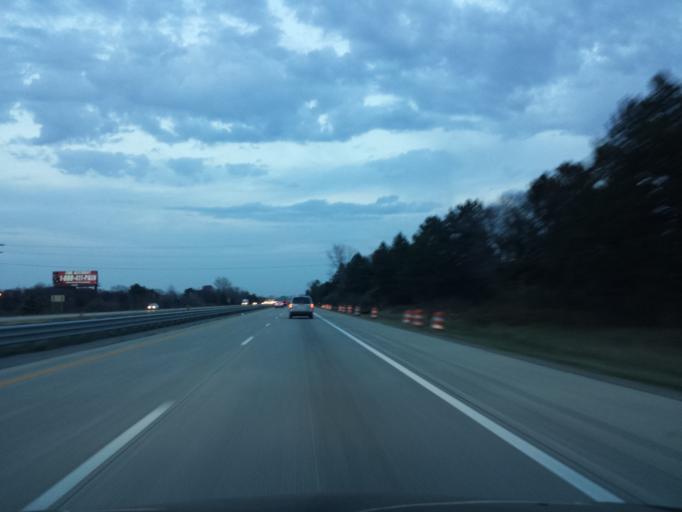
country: US
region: Michigan
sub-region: Genesee County
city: Swartz Creek
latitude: 42.9669
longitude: -83.7832
